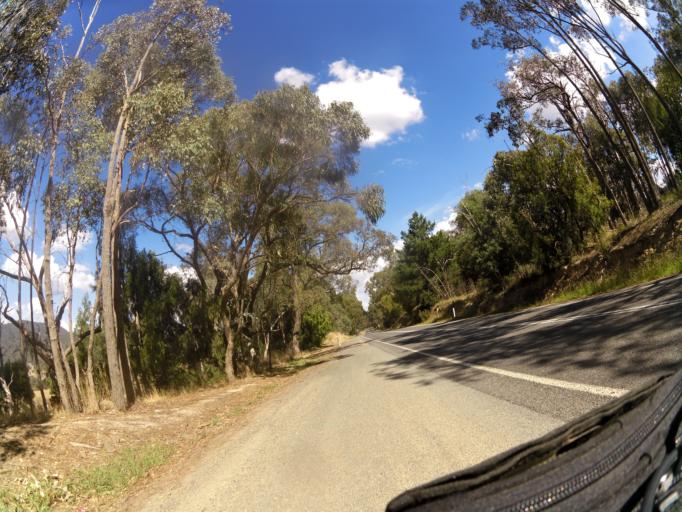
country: AU
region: Victoria
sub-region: Mansfield
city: Mansfield
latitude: -36.8411
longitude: 146.0075
